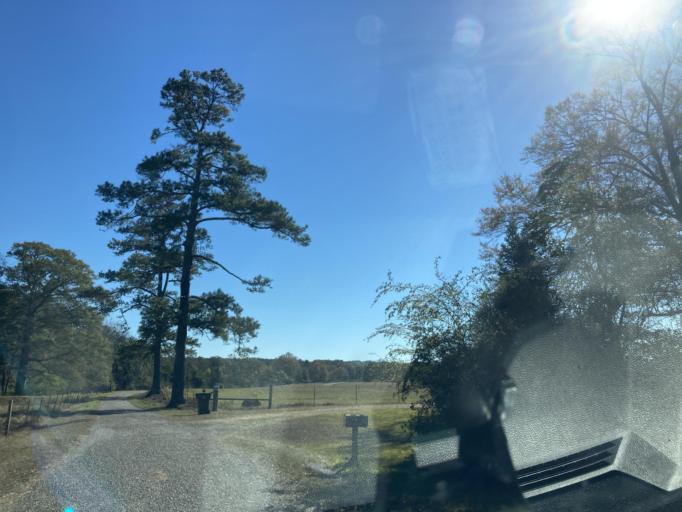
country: US
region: Mississippi
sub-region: Lamar County
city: Sumrall
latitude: 31.3099
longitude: -89.6511
